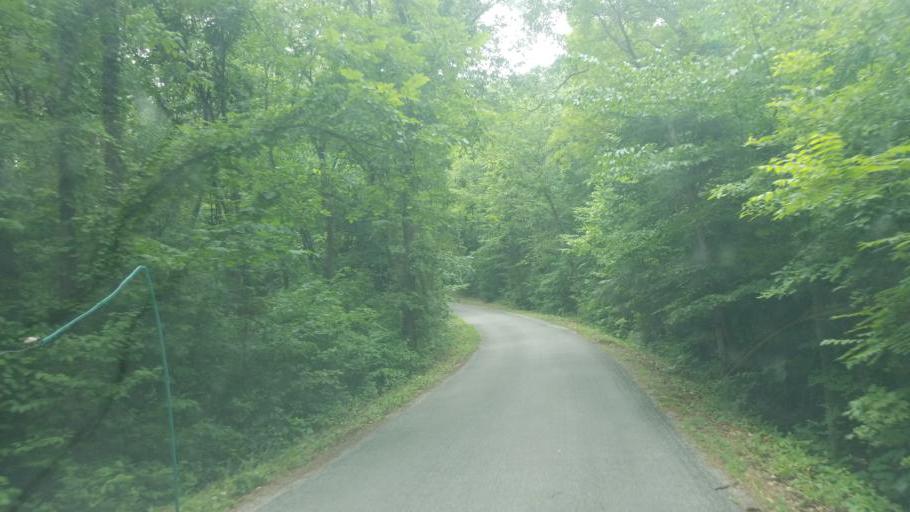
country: US
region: Illinois
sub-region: Jackson County
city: Murphysboro
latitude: 37.6801
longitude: -89.3929
